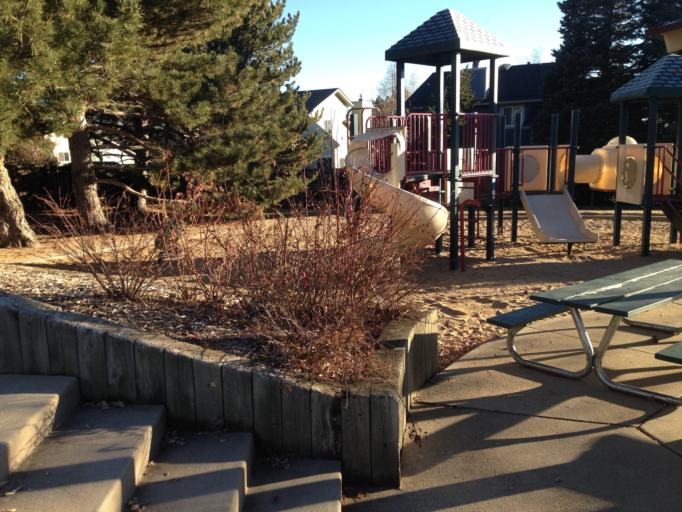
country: US
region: Colorado
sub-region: Boulder County
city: Louisville
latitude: 39.9835
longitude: -105.1614
